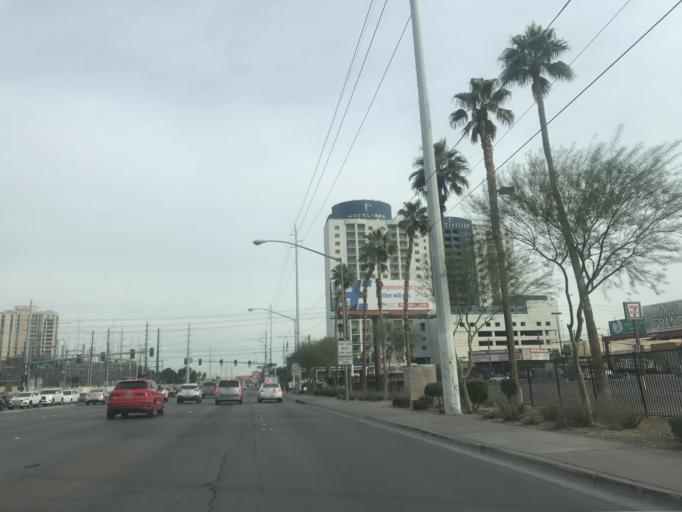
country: US
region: Nevada
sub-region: Clark County
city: Paradise
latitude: 36.1144
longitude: -115.1653
